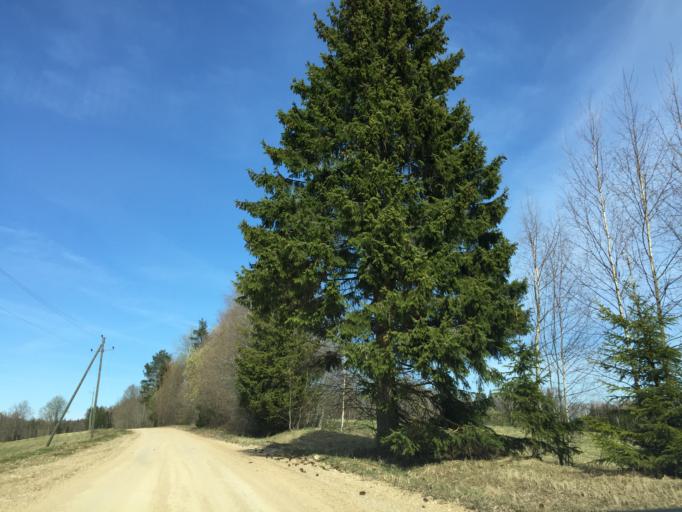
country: EE
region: Vorumaa
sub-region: Antsla vald
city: Vana-Antsla
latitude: 57.9674
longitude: 26.3447
